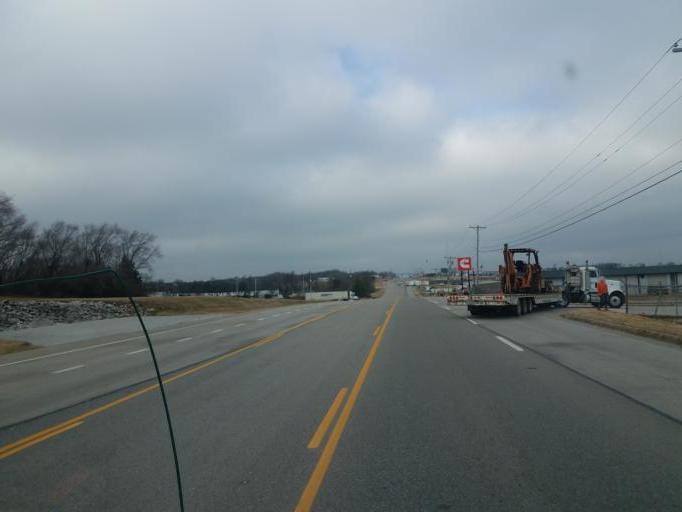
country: US
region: Missouri
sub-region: Greene County
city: Springfield
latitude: 37.2387
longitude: -93.2175
